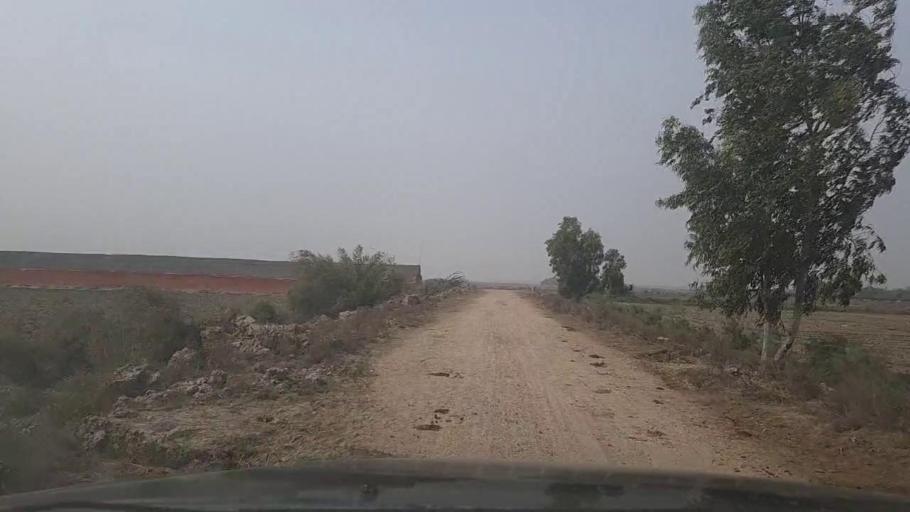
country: PK
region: Sindh
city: Mirpur Sakro
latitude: 24.5304
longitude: 67.7904
